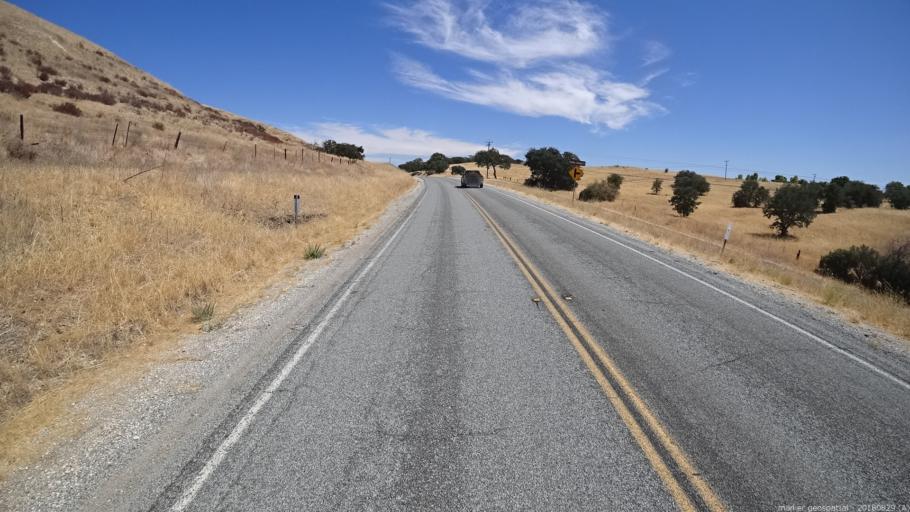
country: US
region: California
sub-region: San Luis Obispo County
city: Lake Nacimiento
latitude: 35.9088
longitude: -121.0144
